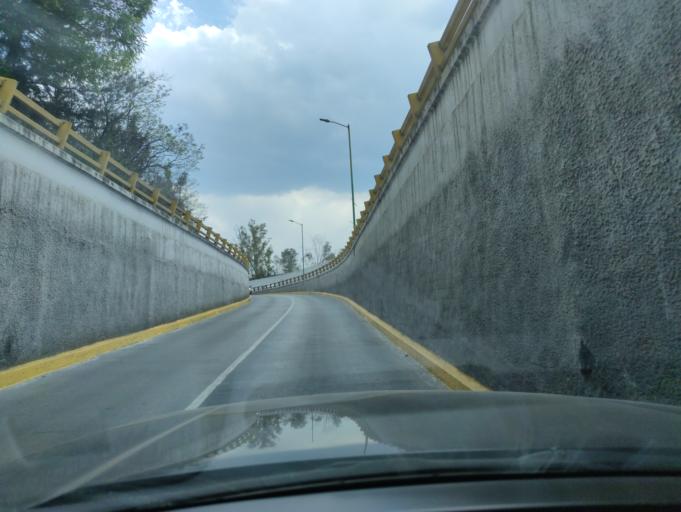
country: MX
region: Mexico
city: Cuautitlan Izcalli
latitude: 19.6261
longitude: -99.2374
